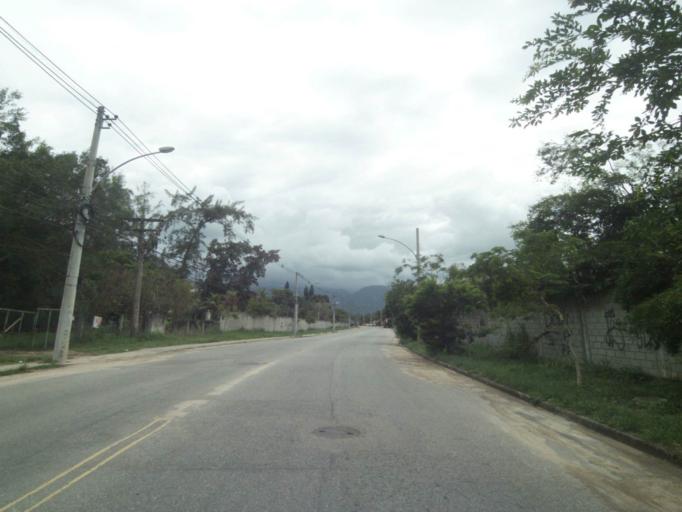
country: BR
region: Rio de Janeiro
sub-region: Nilopolis
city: Nilopolis
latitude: -23.0023
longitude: -43.5102
